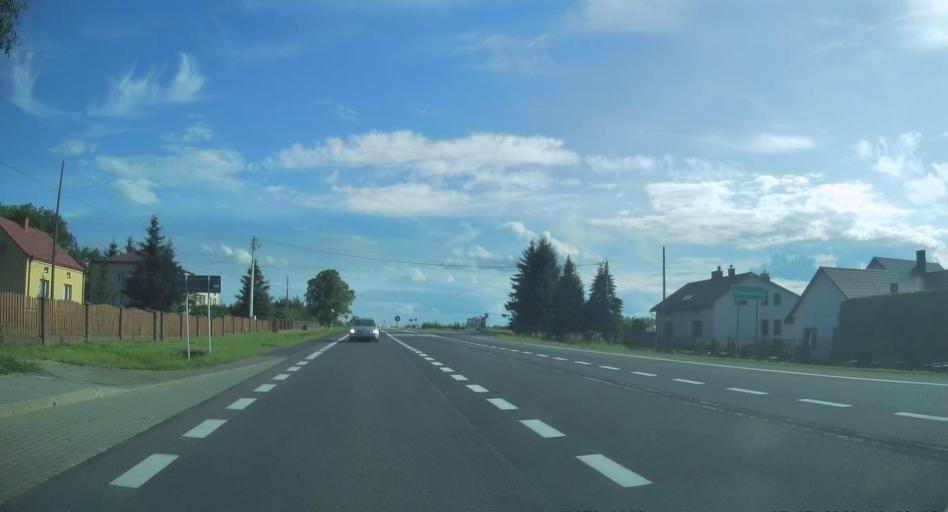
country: PL
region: Subcarpathian Voivodeship
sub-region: Powiat przemyski
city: Orly
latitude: 49.8530
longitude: 22.8051
